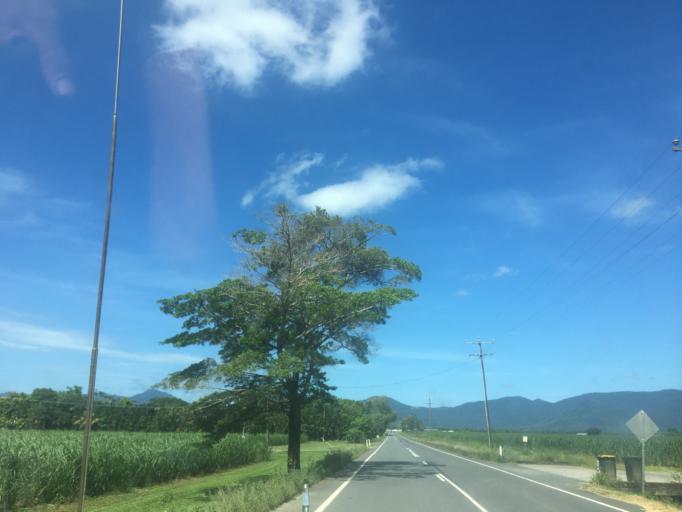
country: AU
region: Queensland
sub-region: Cairns
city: Woree
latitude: -17.0637
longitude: 145.7568
